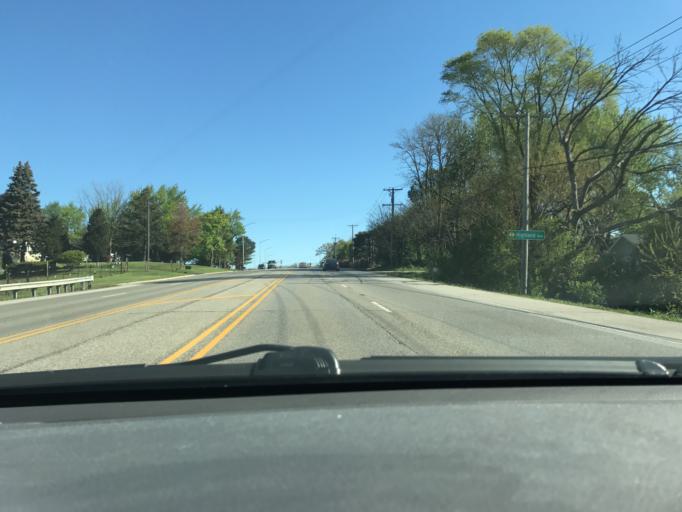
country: US
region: Illinois
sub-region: Kane County
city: Elgin
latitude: 42.0450
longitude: -88.3411
